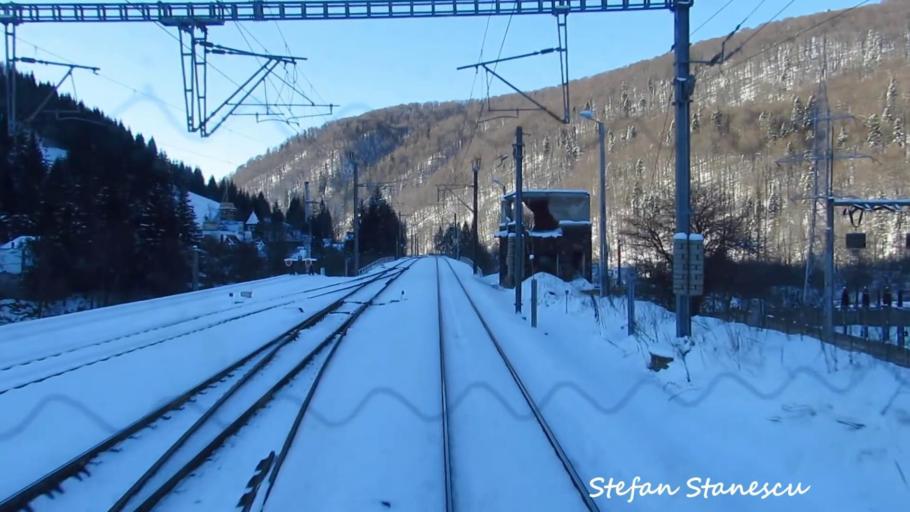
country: RO
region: Prahova
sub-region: Oras Azuga
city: Azuga
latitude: 45.4348
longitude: 25.5514
